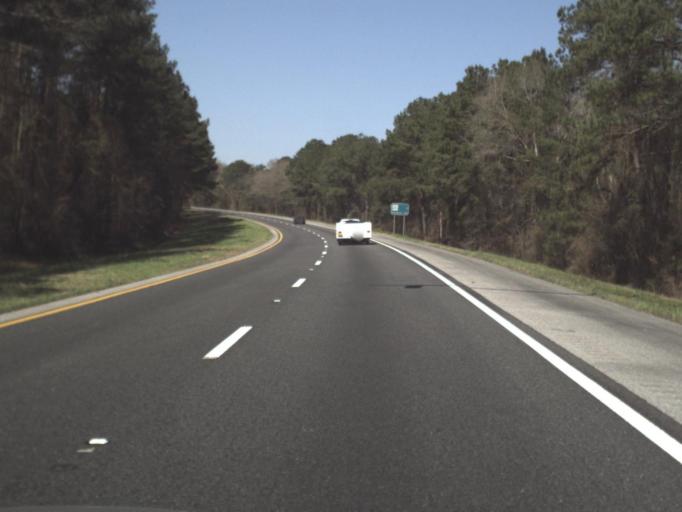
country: US
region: Florida
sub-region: Jackson County
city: Sneads
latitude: 30.6406
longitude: -84.9610
